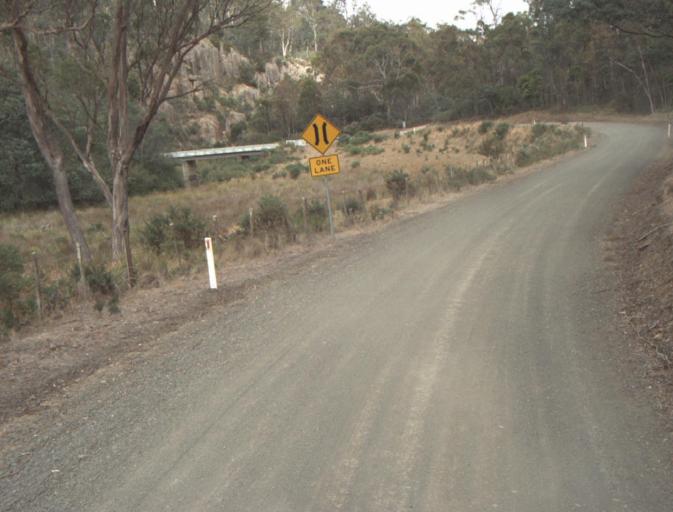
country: AU
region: Tasmania
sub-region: Northern Midlands
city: Evandale
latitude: -41.4923
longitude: 147.4339
